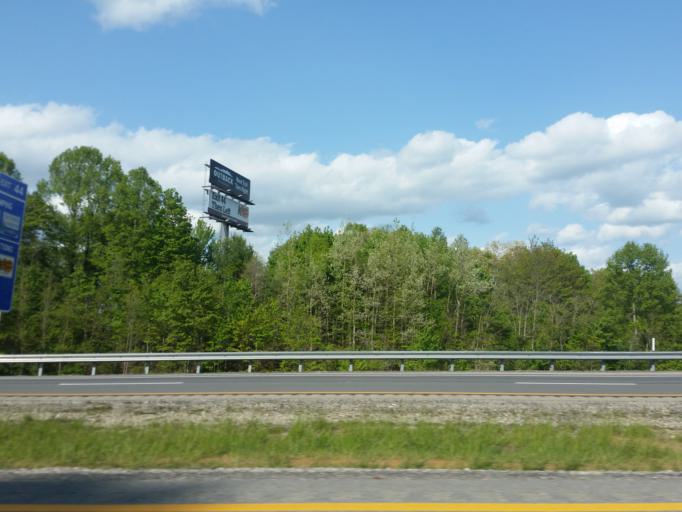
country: US
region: West Virginia
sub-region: Raleigh County
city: MacArthur
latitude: 37.7630
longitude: -81.2153
